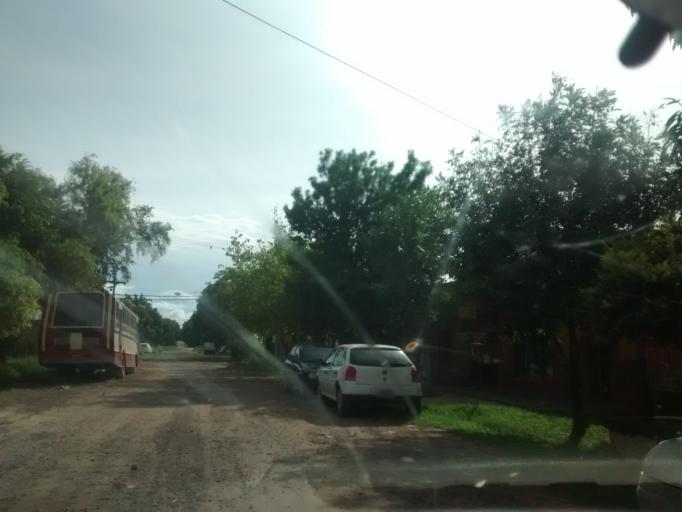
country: AR
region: Chaco
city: Fontana
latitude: -27.4396
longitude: -59.0058
